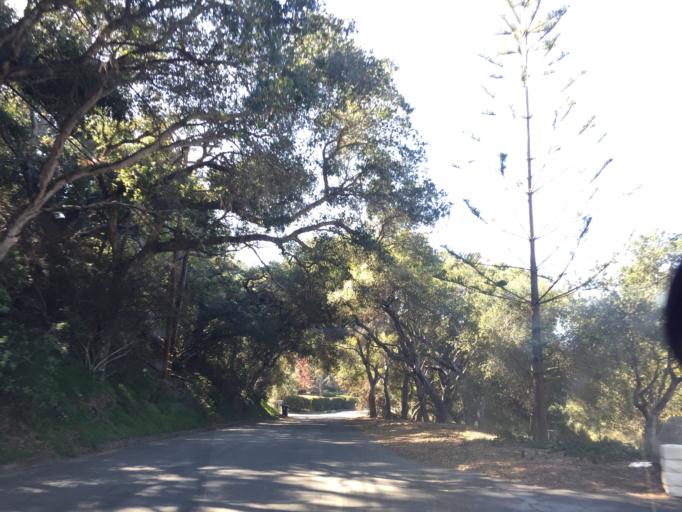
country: US
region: California
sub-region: Santa Barbara County
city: Goleta
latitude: 34.4326
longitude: -119.7757
